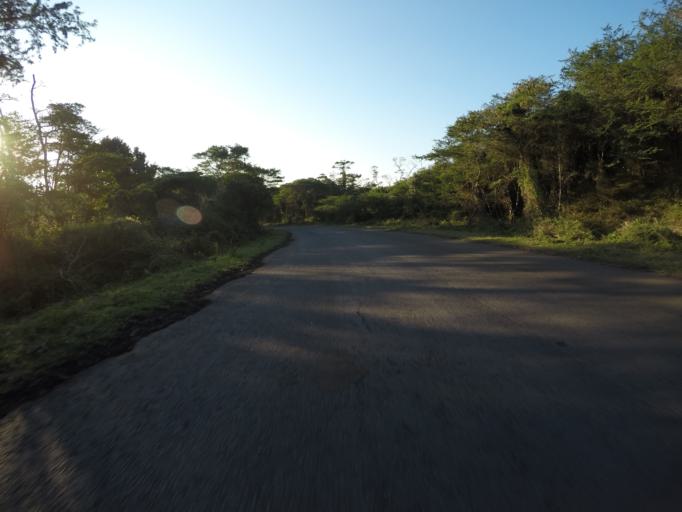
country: ZA
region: KwaZulu-Natal
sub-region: uThungulu District Municipality
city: KwaMbonambi
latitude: -28.6945
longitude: 32.2107
